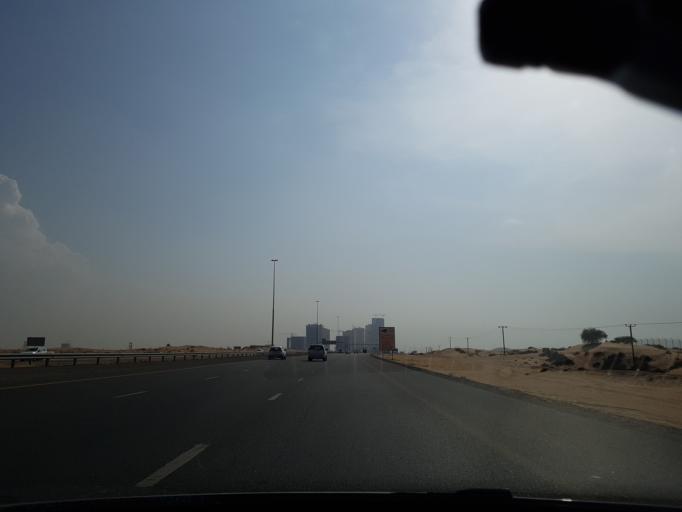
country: AE
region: Ajman
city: Ajman
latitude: 25.4120
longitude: 55.5860
